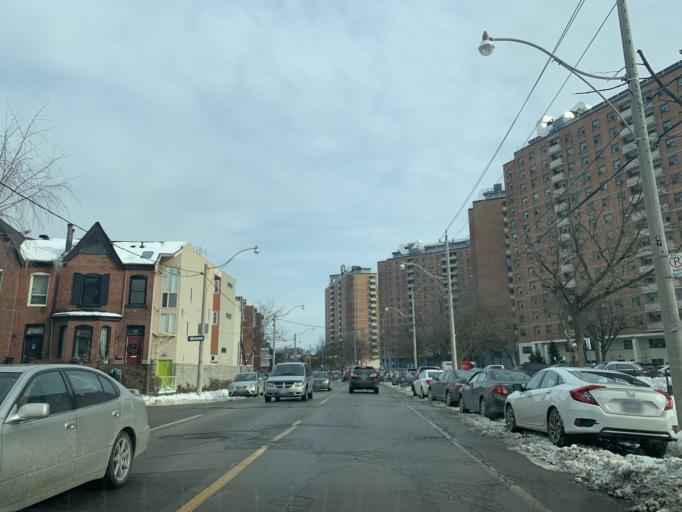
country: CA
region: Ontario
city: Toronto
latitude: 43.6563
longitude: -79.3688
